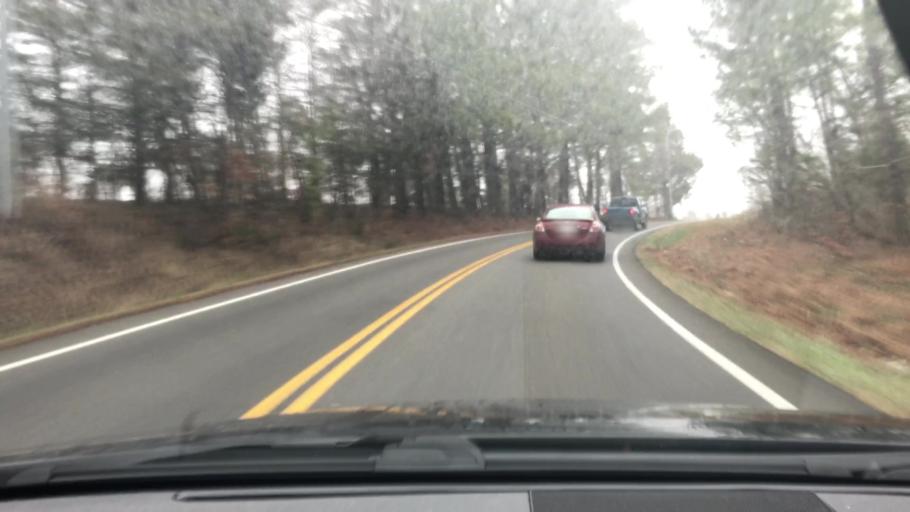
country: US
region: Tennessee
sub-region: Cheatham County
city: Ashland City
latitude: 36.2847
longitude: -87.1805
